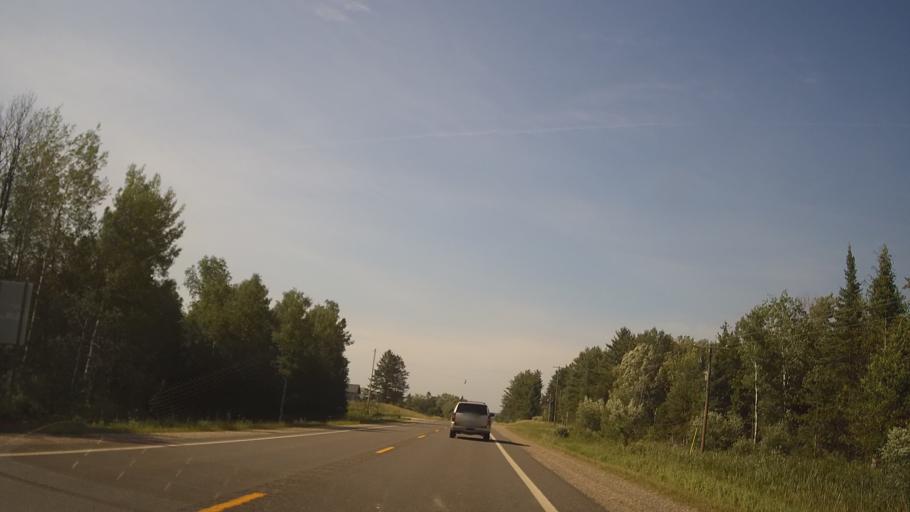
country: US
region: Michigan
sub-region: Ogemaw County
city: West Branch
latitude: 44.3913
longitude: -84.1163
